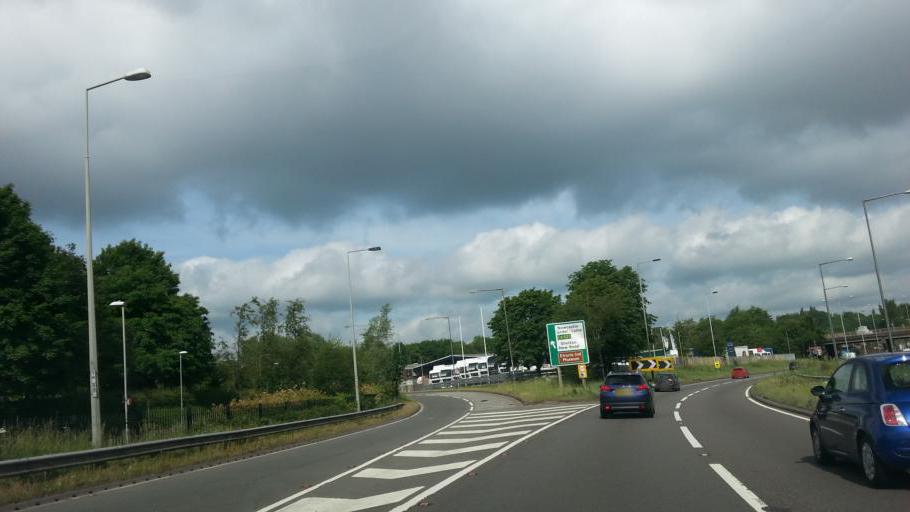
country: GB
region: England
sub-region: Stoke-on-Trent
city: Stoke-on-Trent
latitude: 53.0118
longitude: -2.1966
